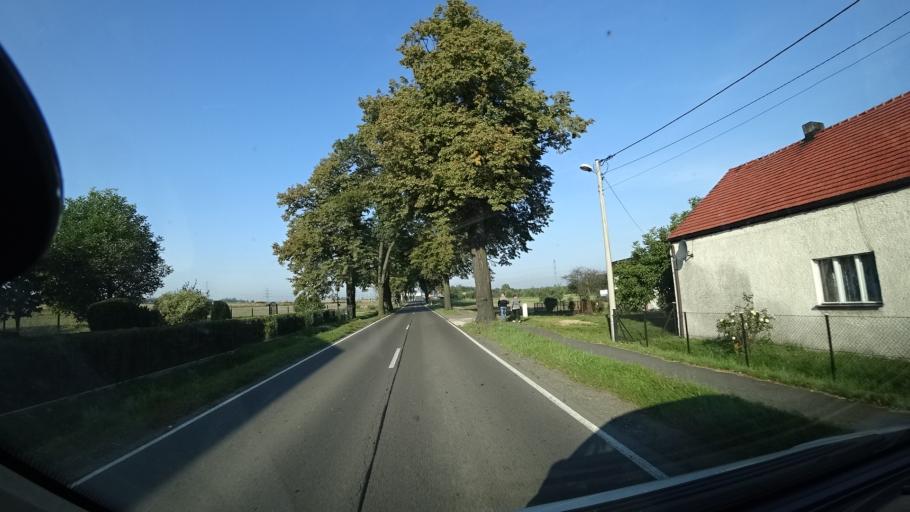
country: PL
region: Silesian Voivodeship
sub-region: Powiat gliwicki
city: Sosnicowice
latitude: 50.2690
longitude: 18.5535
